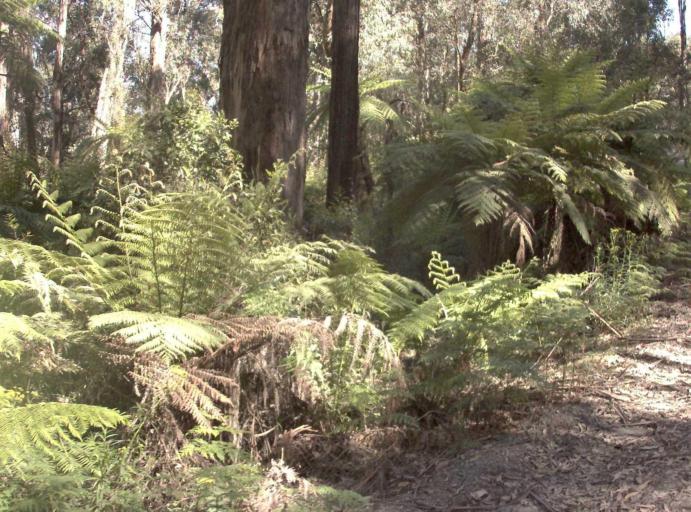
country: AU
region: New South Wales
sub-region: Bombala
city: Bombala
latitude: -37.2490
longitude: 148.7479
